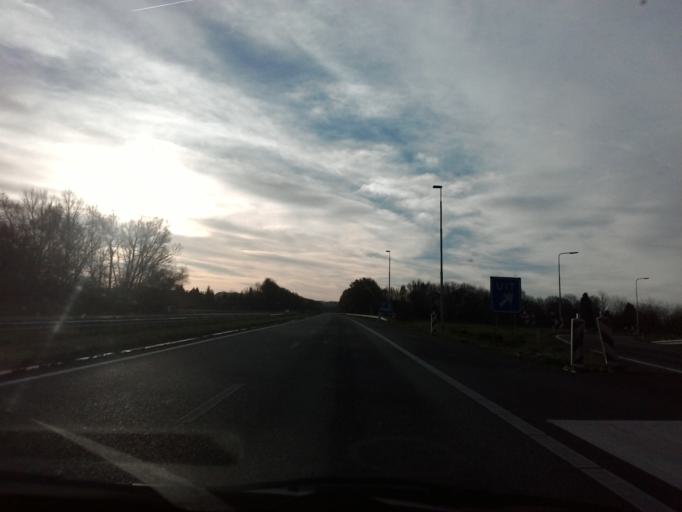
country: NL
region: Limburg
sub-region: Eijsden-Margraten
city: Eijsden
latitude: 50.7932
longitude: 5.7258
